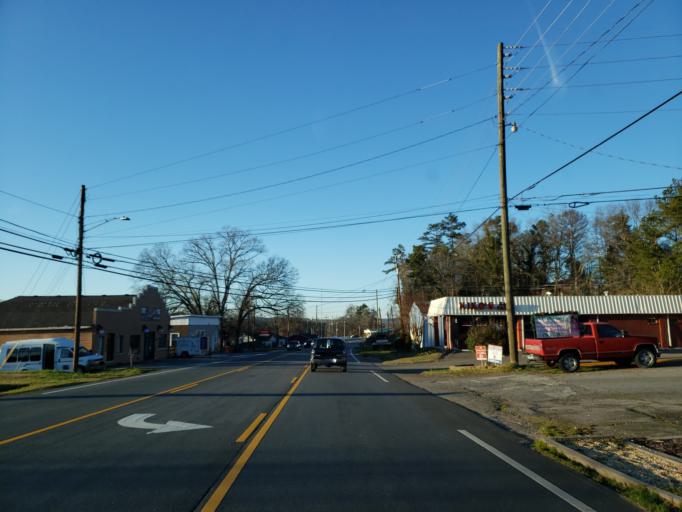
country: US
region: Georgia
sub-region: Cherokee County
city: Canton
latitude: 34.2138
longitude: -84.5045
